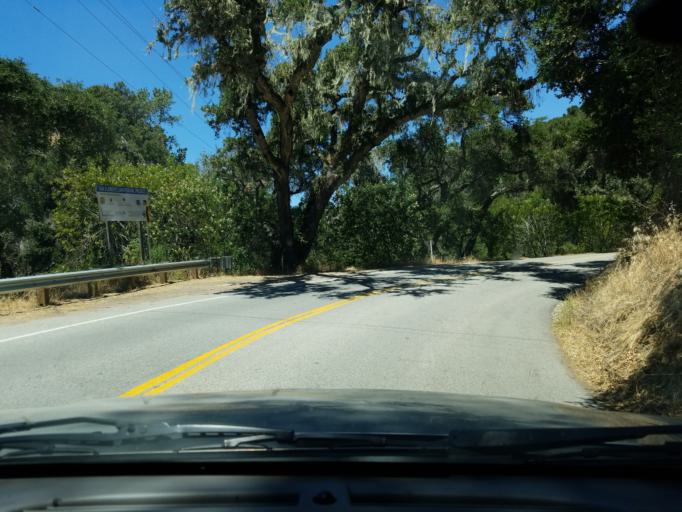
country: US
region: California
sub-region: Monterey County
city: Carmel Valley Village
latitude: 36.4602
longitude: -121.7089
